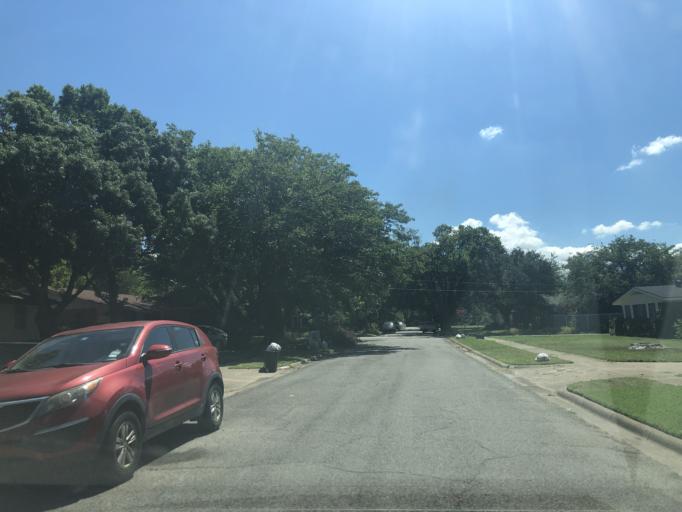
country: US
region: Texas
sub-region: Dallas County
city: Duncanville
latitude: 32.6527
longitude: -96.9141
